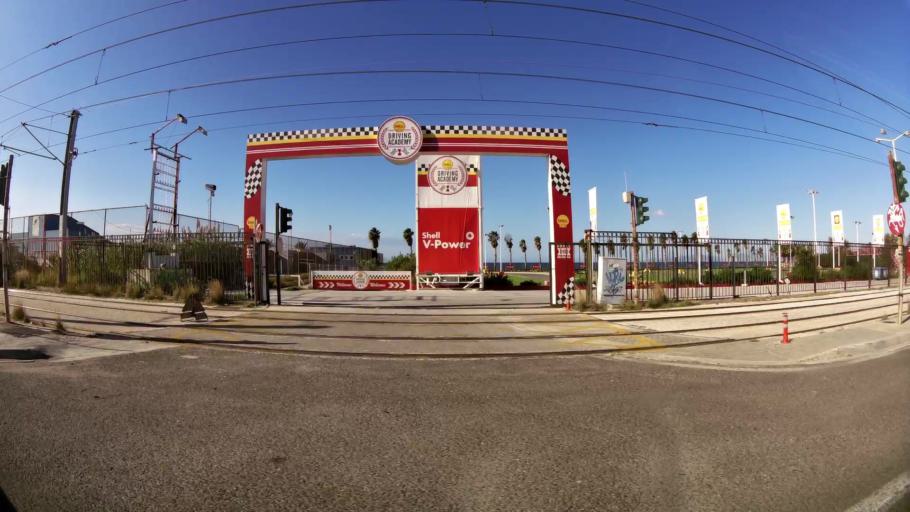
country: GR
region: Attica
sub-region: Nomarchia Athinas
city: Elliniko
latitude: 37.8886
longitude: 23.7247
